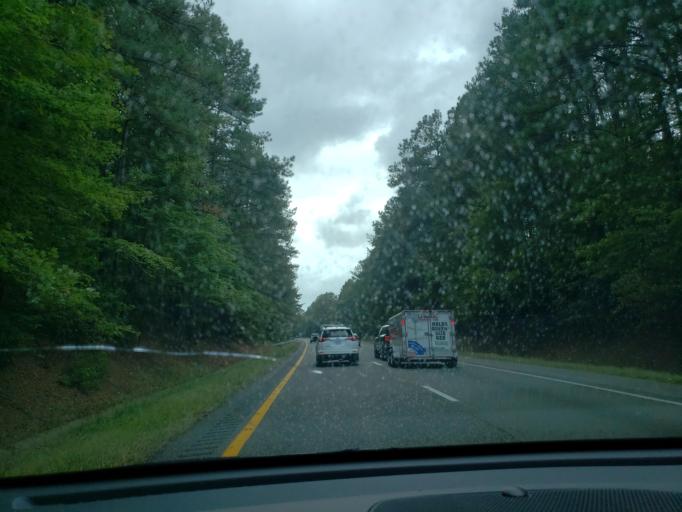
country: US
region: Virginia
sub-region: Brunswick County
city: Lawrenceville
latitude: 36.8176
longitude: -77.9680
